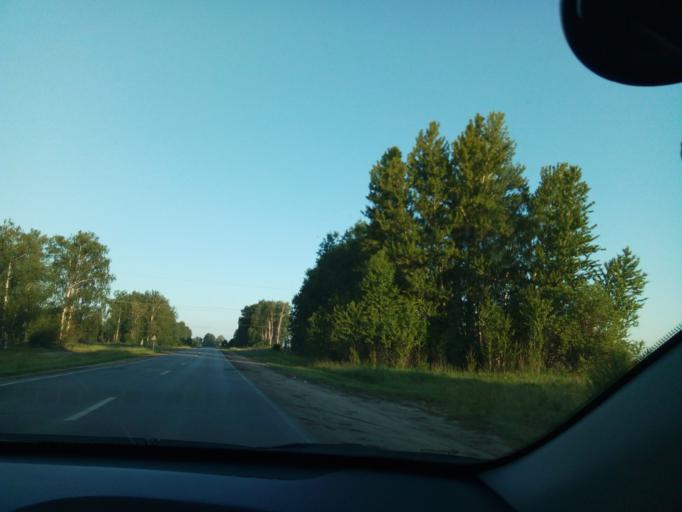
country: RU
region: Nizjnij Novgorod
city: Satis
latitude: 54.9384
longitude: 43.2564
